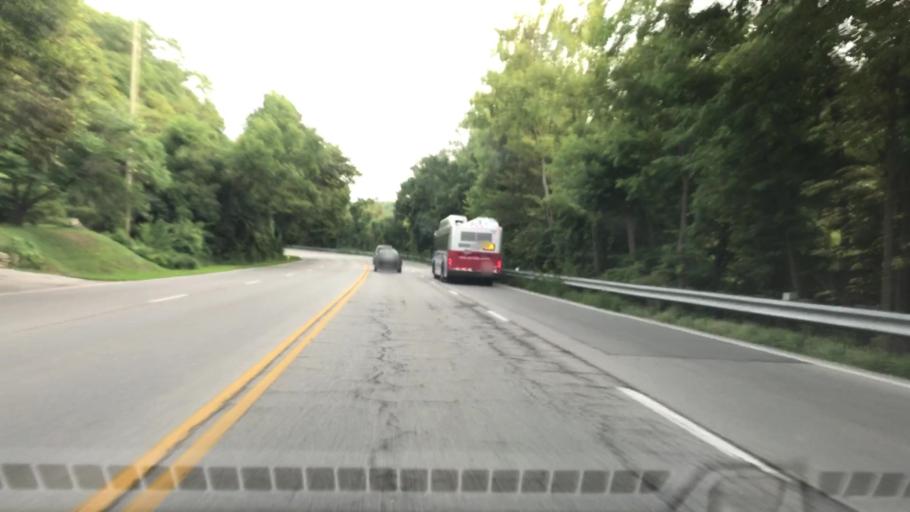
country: US
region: Ohio
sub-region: Franklin County
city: Upper Arlington
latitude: 40.0147
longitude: -83.0904
